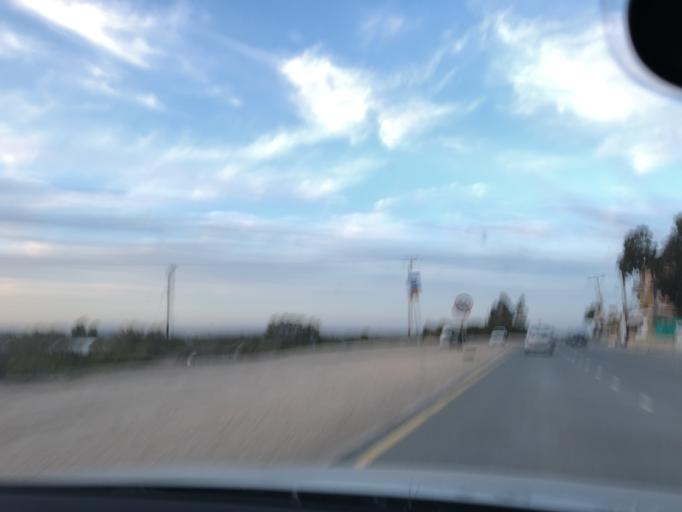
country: CY
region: Larnaka
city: Meneou
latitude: 34.8438
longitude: 33.6147
